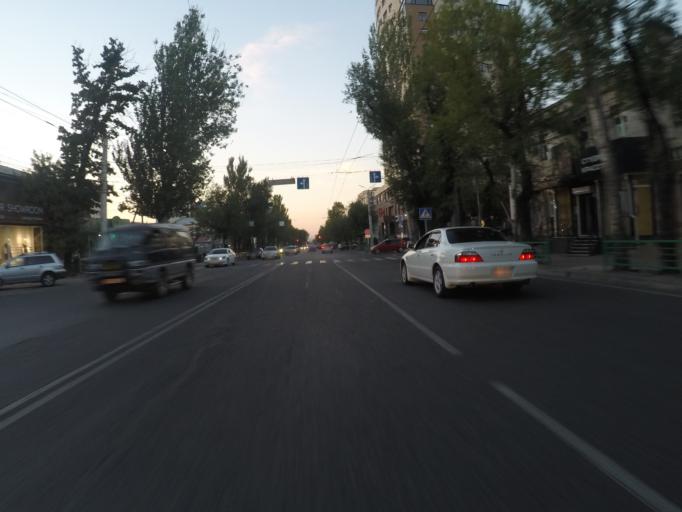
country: KG
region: Chuy
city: Bishkek
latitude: 42.8545
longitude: 74.6101
